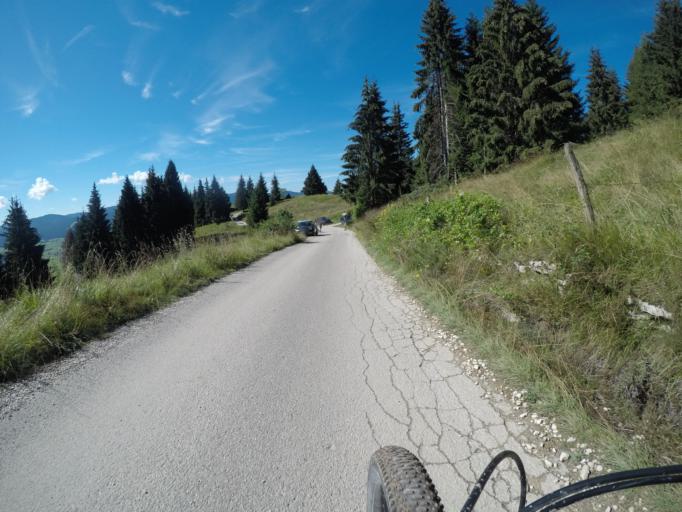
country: IT
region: Veneto
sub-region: Provincia di Vicenza
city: Canove di Roana
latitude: 45.8910
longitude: 11.4833
